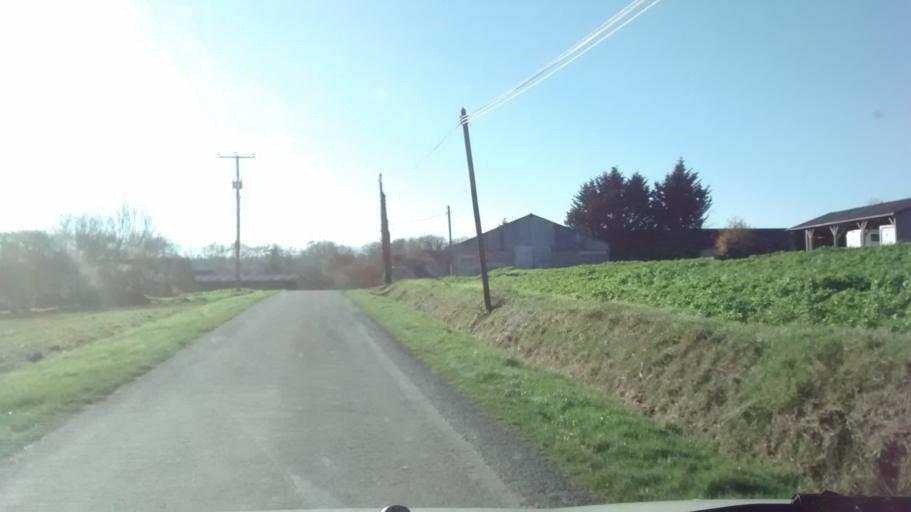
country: FR
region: Brittany
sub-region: Departement d'Ille-et-Vilaine
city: La Bouexiere
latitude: 48.2019
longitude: -1.4604
